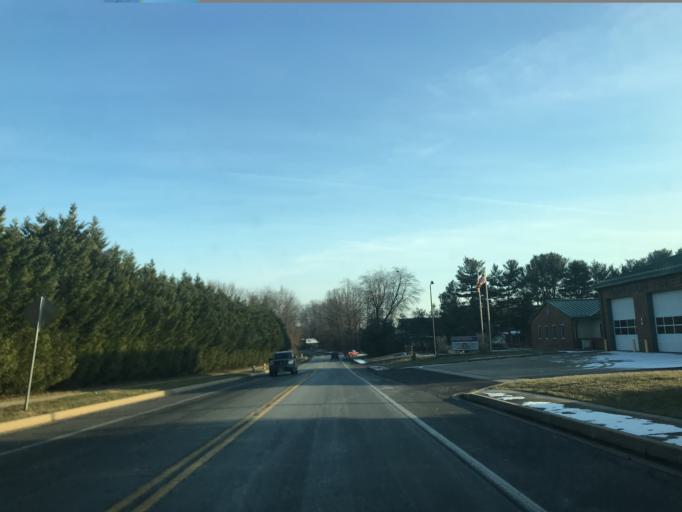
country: US
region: Maryland
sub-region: Harford County
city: Edgewood
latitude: 39.4332
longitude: -76.2708
